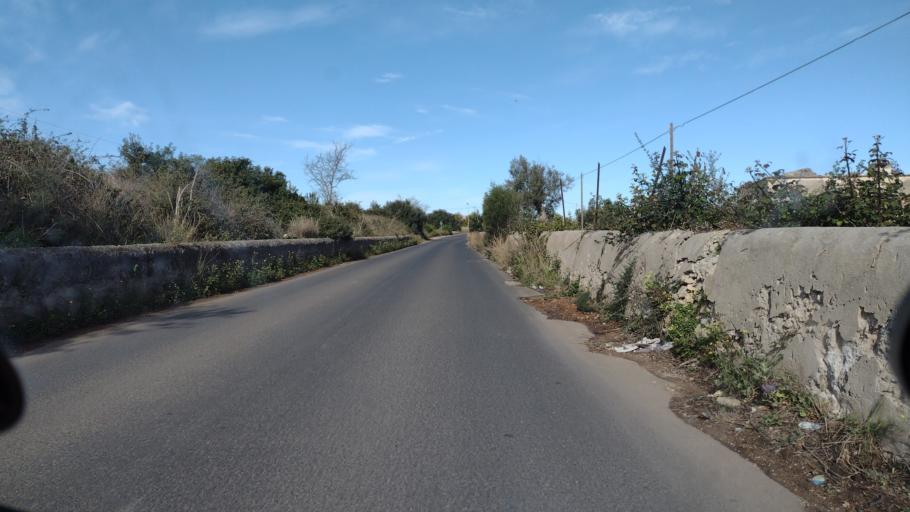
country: IT
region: Sicily
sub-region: Provincia di Siracusa
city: Avola
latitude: 36.8733
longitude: 15.1181
